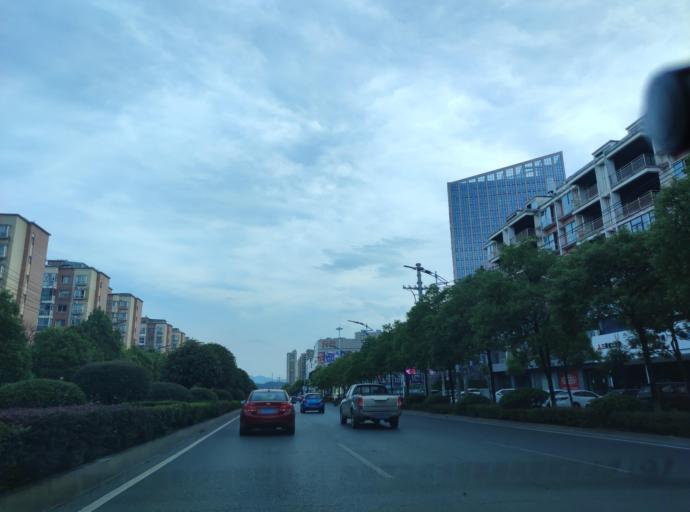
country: CN
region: Jiangxi Sheng
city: Pingxiang
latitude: 27.6388
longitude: 113.8704
